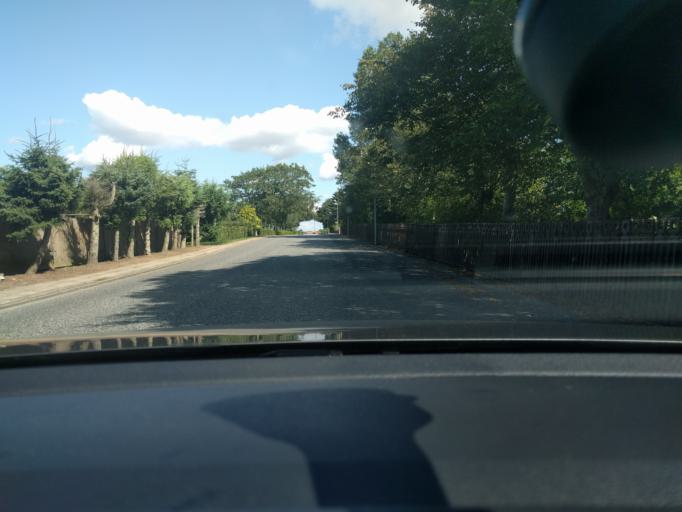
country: DK
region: Central Jutland
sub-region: Viborg Kommune
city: Viborg
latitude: 56.5509
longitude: 9.4010
